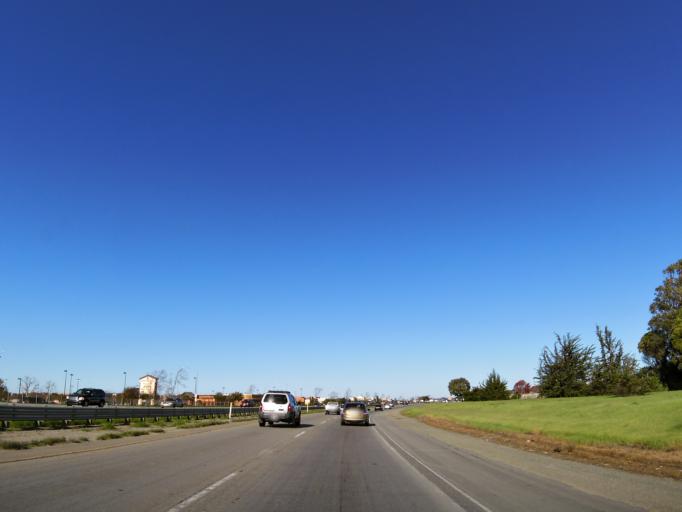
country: US
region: California
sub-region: Monterey County
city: Boronda
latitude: 36.7036
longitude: -121.6663
